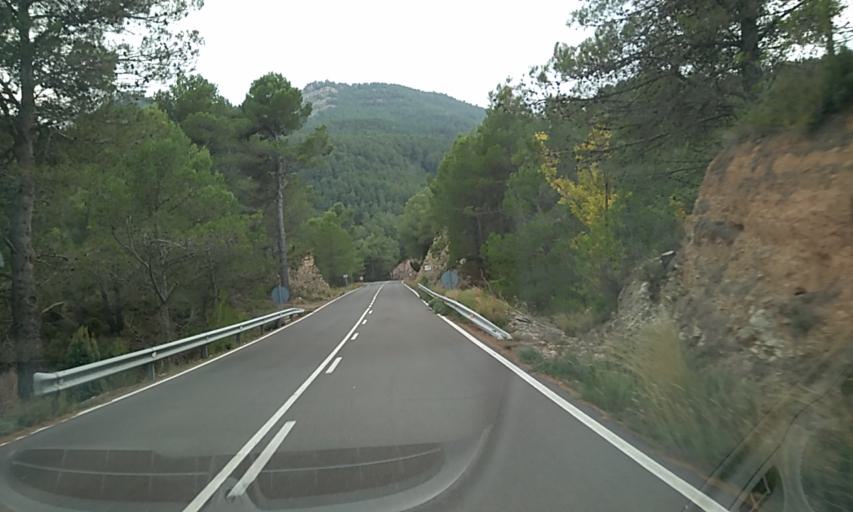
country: ES
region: Valencia
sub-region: Provincia de Castello
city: Puebla de Arenoso
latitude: 40.0957
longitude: -0.5731
